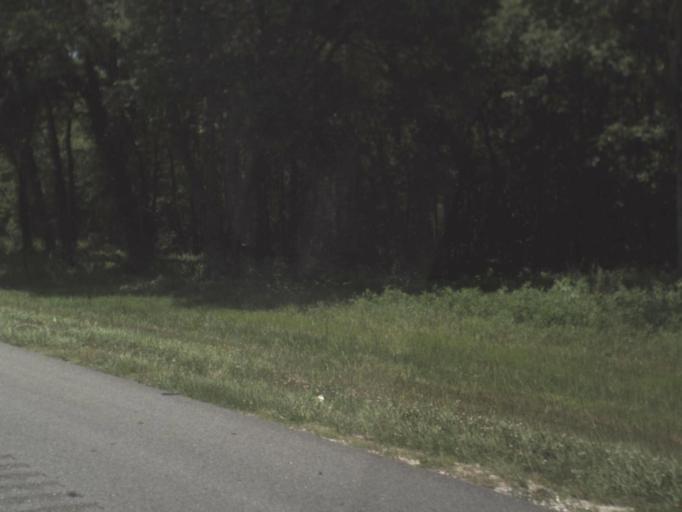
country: US
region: Florida
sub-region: Columbia County
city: Five Points
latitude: 30.2451
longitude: -82.6805
